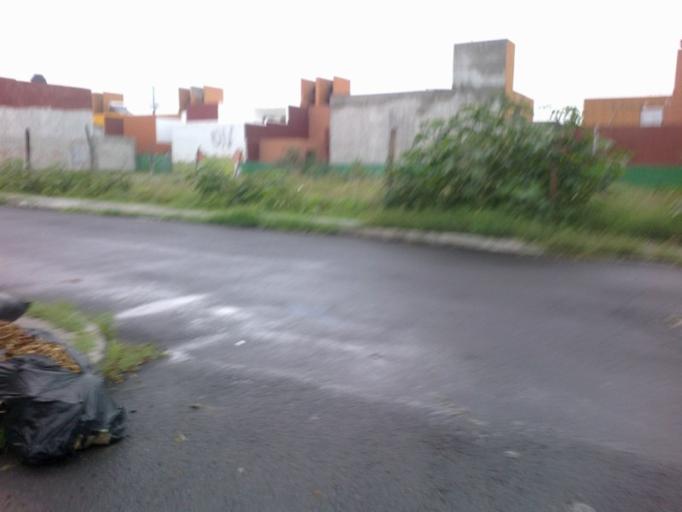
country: MX
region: Queretaro
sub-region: Queretaro
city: Sergio Villasenor
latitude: 20.6253
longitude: -100.4033
